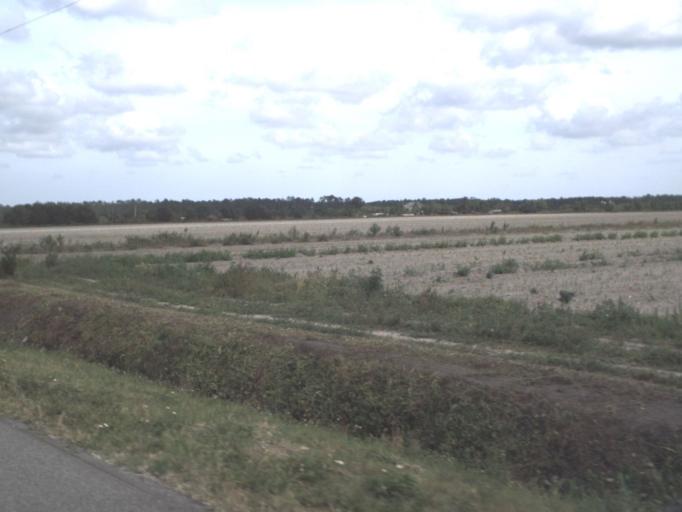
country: US
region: Florida
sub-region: Flagler County
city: Bunnell
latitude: 29.4821
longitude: -81.3617
